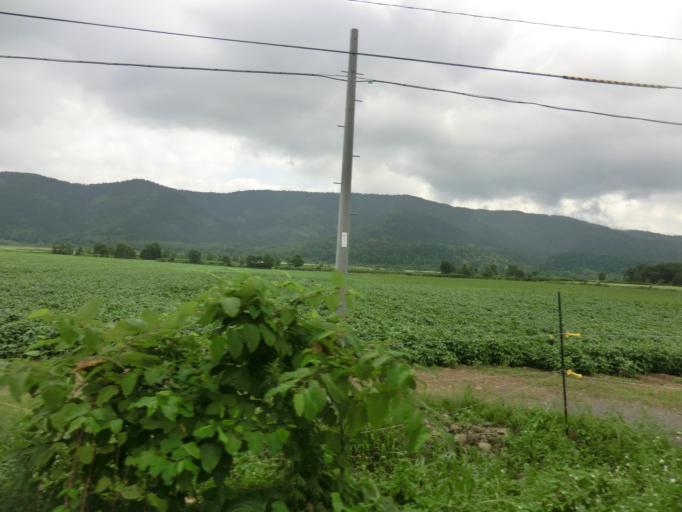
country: JP
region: Hokkaido
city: Nayoro
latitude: 44.1484
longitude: 142.1491
